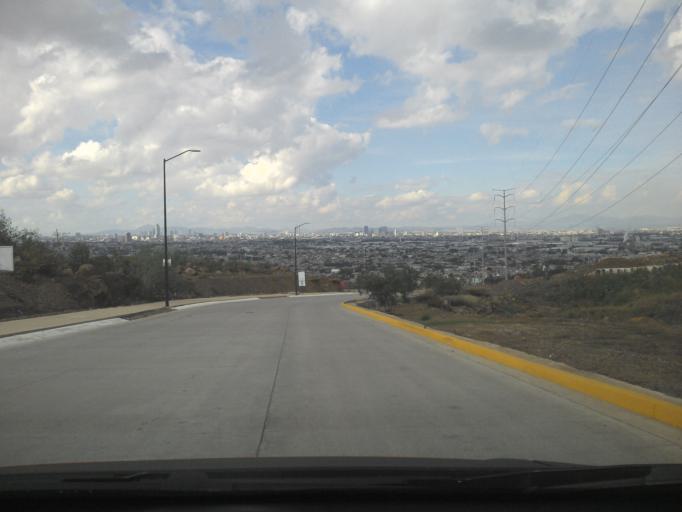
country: MX
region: Jalisco
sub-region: Tlajomulco de Zuniga
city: Altus Bosques
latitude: 20.6098
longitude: -103.3634
